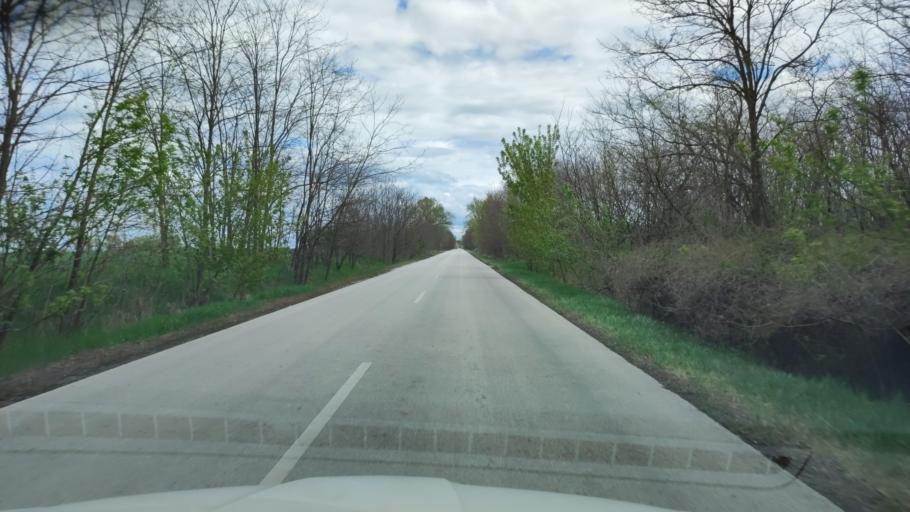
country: HU
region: Pest
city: Tortel
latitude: 47.0627
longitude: 19.9755
